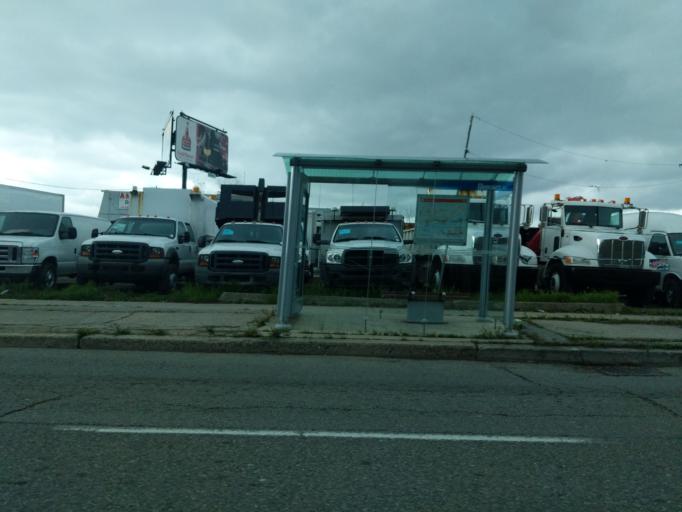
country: CA
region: Ontario
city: Toronto
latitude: 43.7049
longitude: -79.4649
